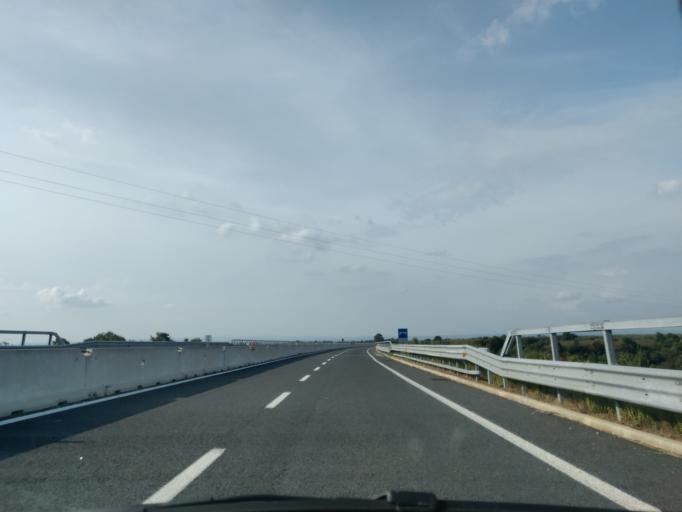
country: IT
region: Latium
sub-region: Provincia di Viterbo
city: Blera
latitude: 42.3294
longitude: 11.9858
